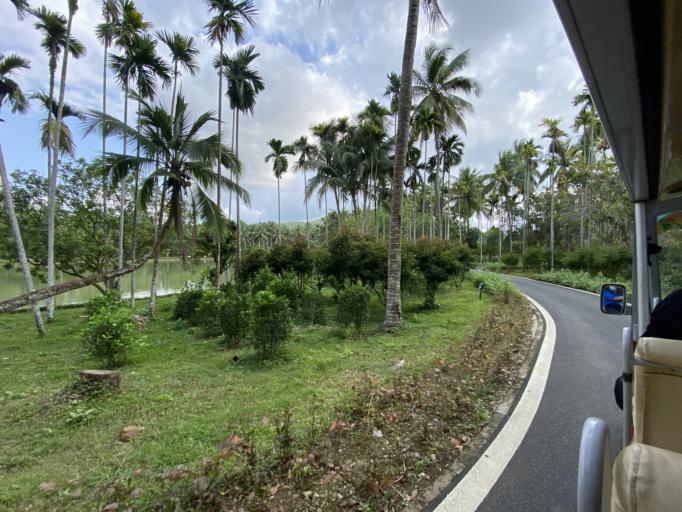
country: CN
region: Hainan
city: Nanqiao
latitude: 18.7340
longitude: 110.1913
